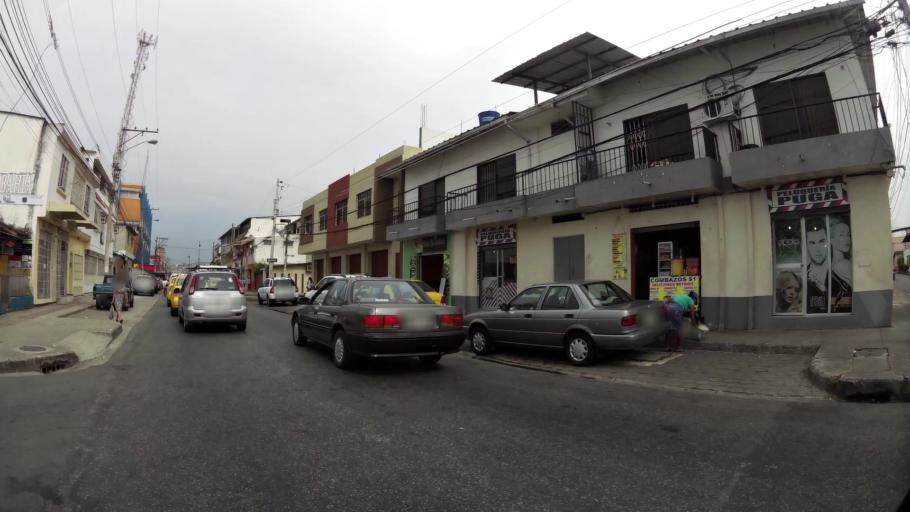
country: EC
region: Guayas
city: Eloy Alfaro
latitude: -2.1387
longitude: -79.8975
